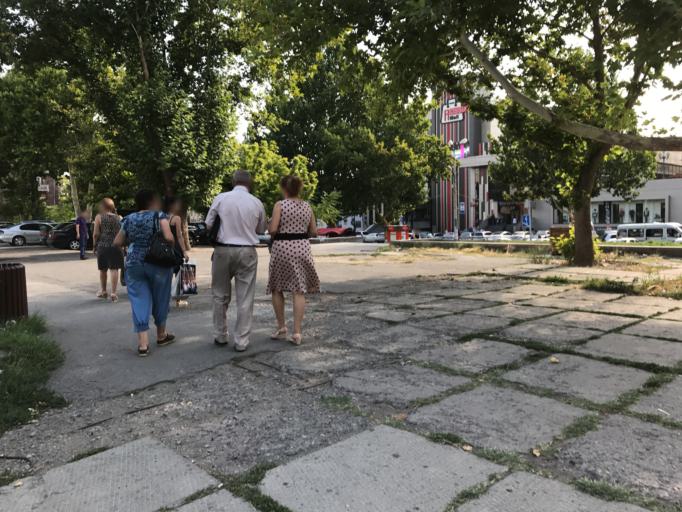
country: AM
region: Yerevan
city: Yerevan
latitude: 40.1722
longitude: 44.5142
